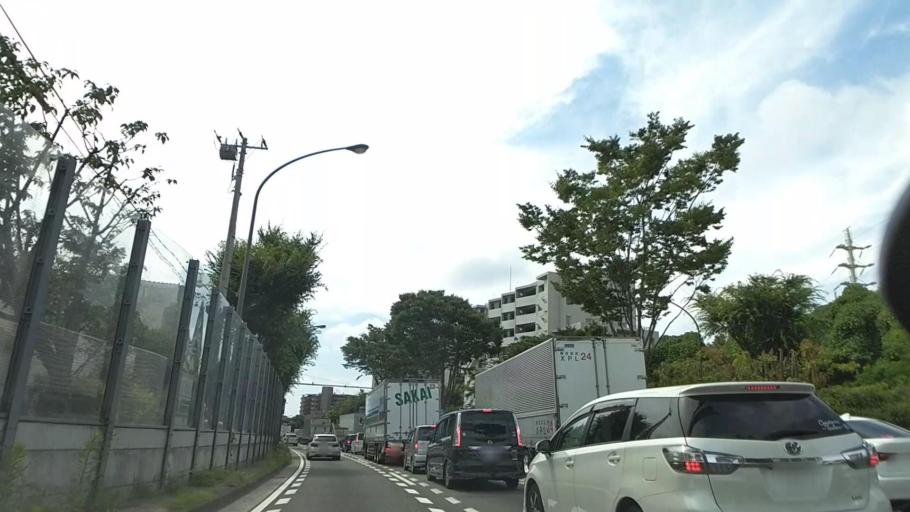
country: JP
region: Kanagawa
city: Yokohama
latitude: 35.4374
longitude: 139.5611
